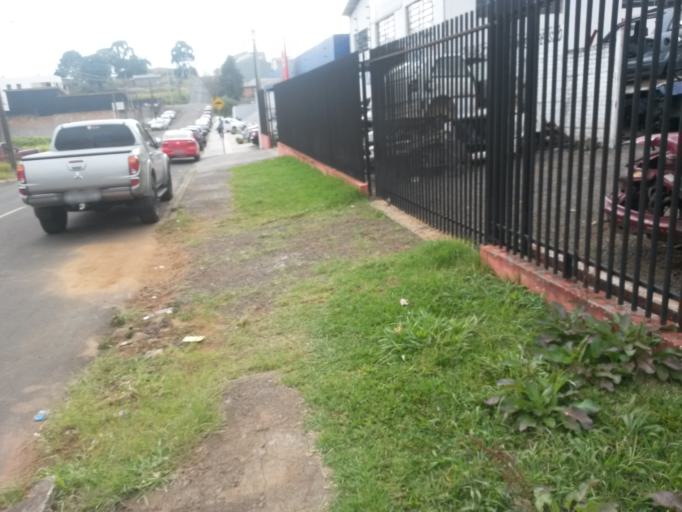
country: BR
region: Parana
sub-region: Guarapuava
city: Guarapuava
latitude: -25.3852
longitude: -51.4559
